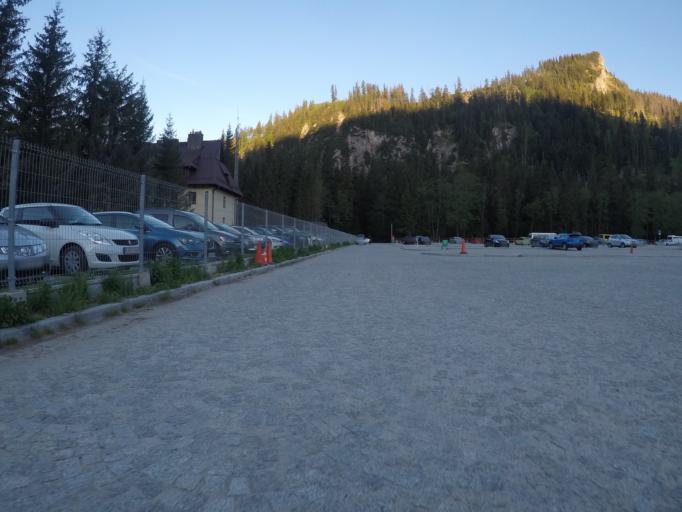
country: PL
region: Lesser Poland Voivodeship
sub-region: Powiat tatrzanski
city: Bukowina Tatrzanska
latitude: 49.2564
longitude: 20.1029
